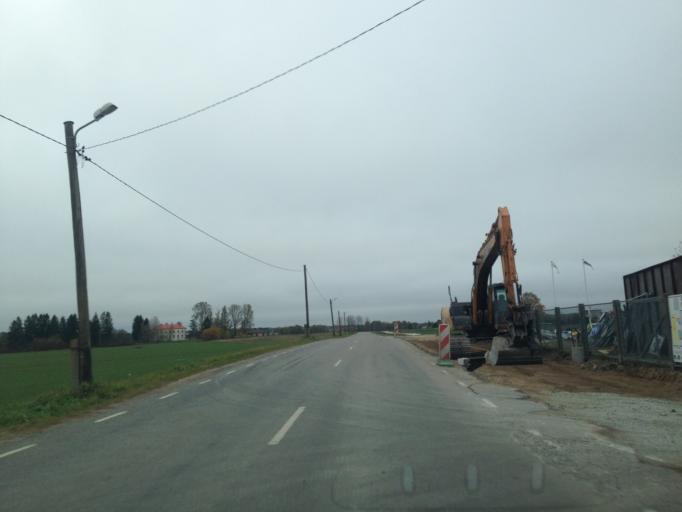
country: EE
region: Harju
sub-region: Saue linn
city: Saue
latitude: 59.3407
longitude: 24.5550
